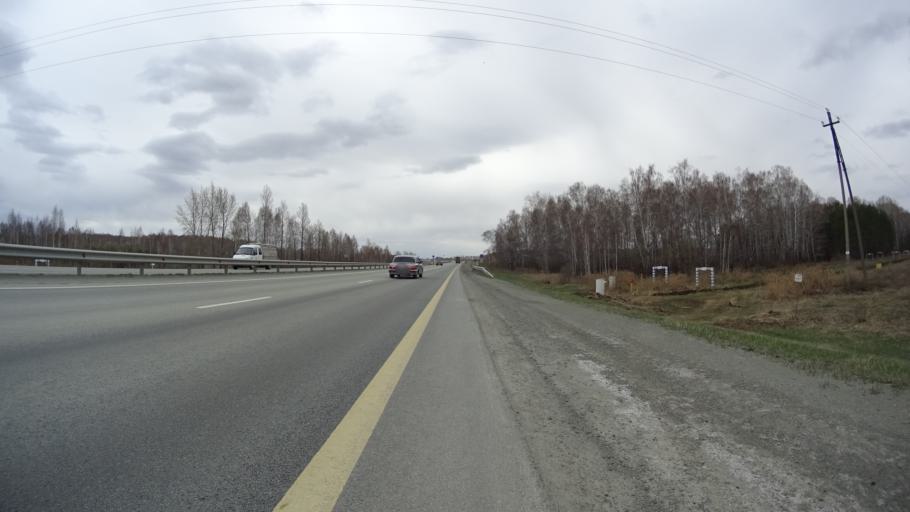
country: RU
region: Chelyabinsk
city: Yemanzhelinka
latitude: 54.8280
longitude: 61.3108
